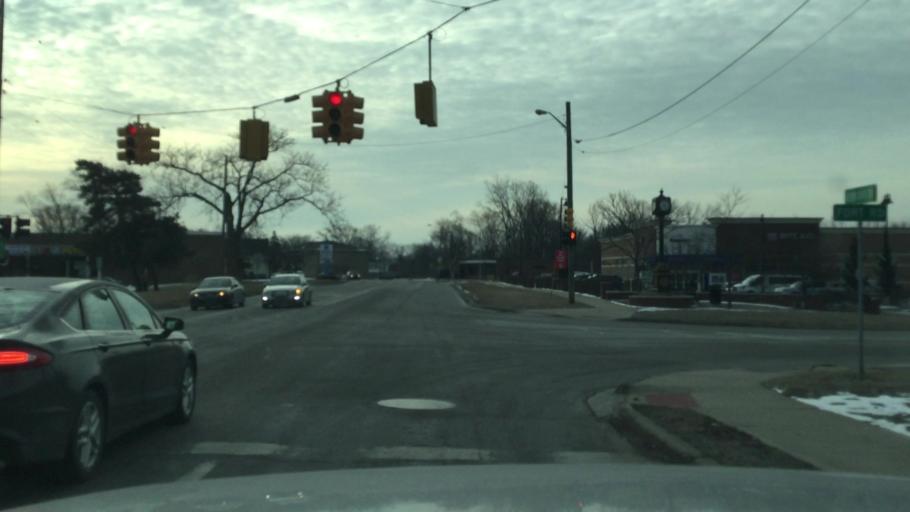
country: US
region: Michigan
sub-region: Wayne County
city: Rockwood
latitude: 42.0685
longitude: -83.2502
